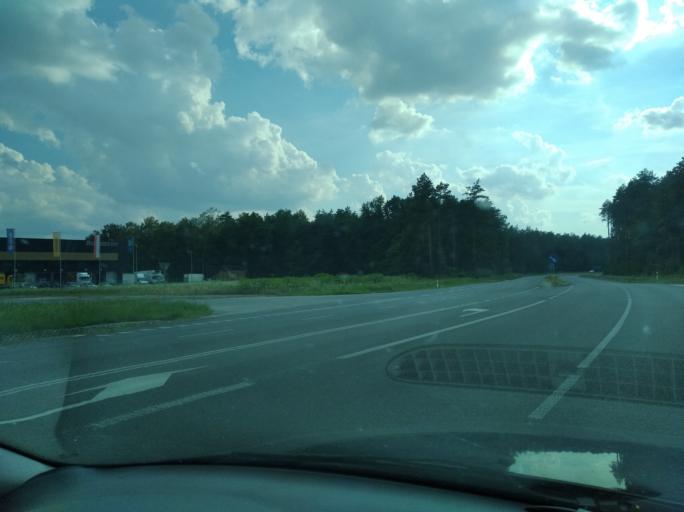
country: PL
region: Subcarpathian Voivodeship
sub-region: Powiat rzeszowski
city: Rudna Mala
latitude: 50.1147
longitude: 21.9984
